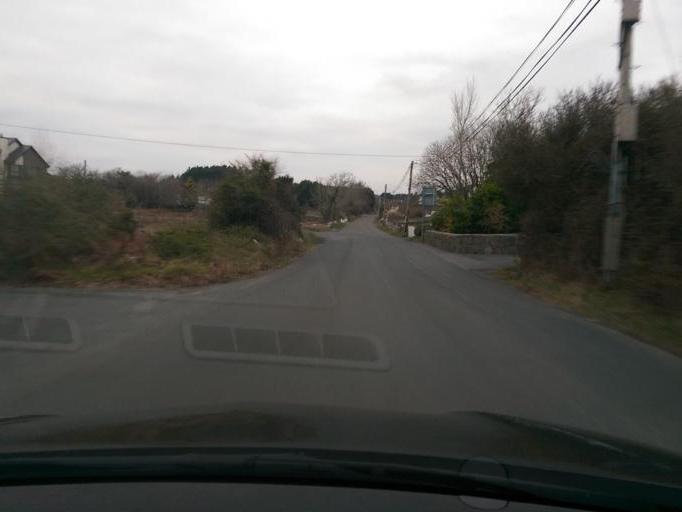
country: IE
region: Connaught
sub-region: County Galway
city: Bearna
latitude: 53.2527
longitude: -9.1530
